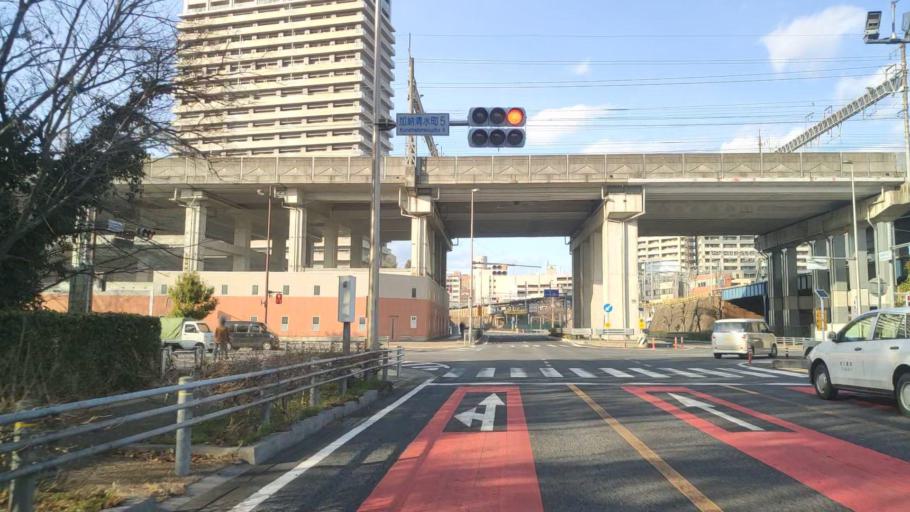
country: JP
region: Gifu
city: Gifu-shi
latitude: 35.4084
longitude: 136.7600
